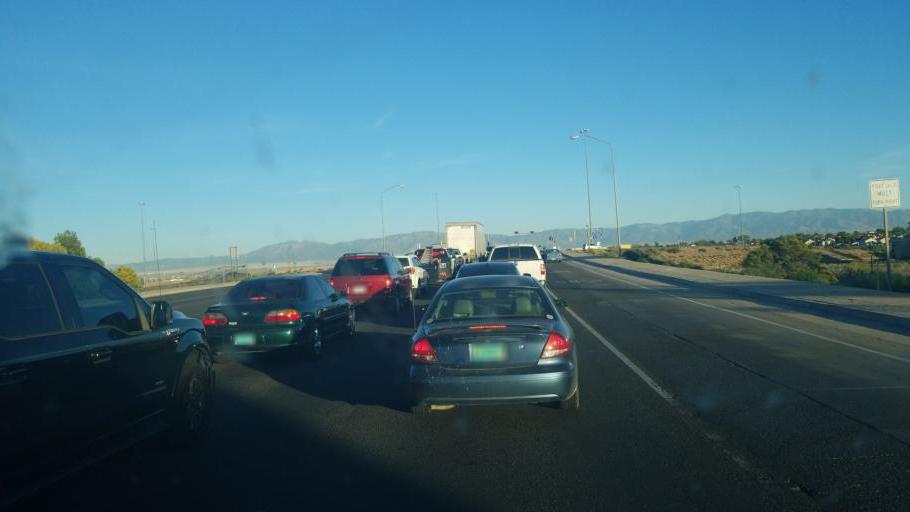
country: US
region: New Mexico
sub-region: Valencia County
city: Los Lunas
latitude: 34.8152
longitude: -106.7641
